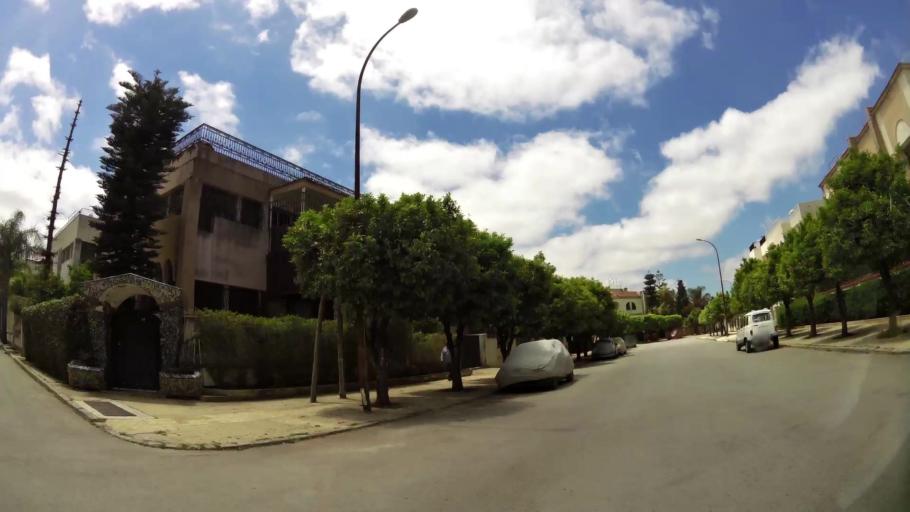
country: MA
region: Fes-Boulemane
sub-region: Fes
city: Fes
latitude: 34.0363
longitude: -5.0196
